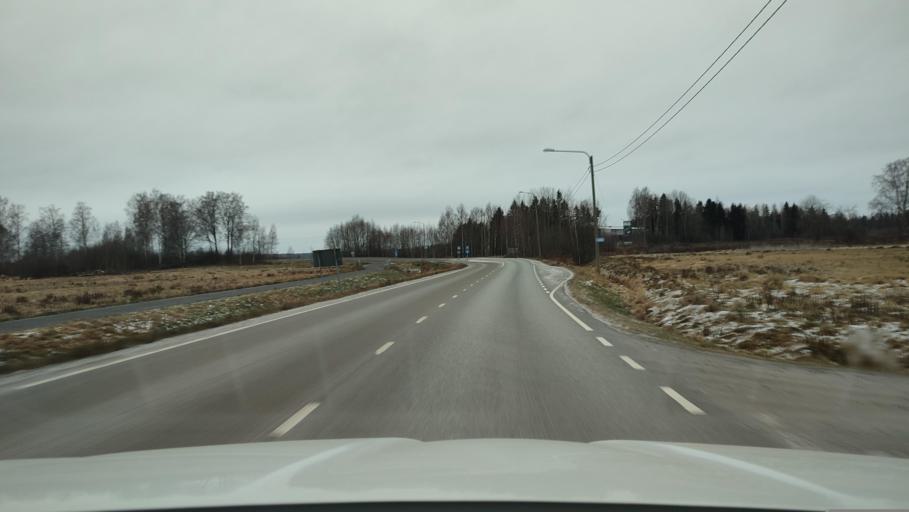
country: FI
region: Ostrobothnia
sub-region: Vaasa
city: Ristinummi
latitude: 63.0358
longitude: 21.7848
